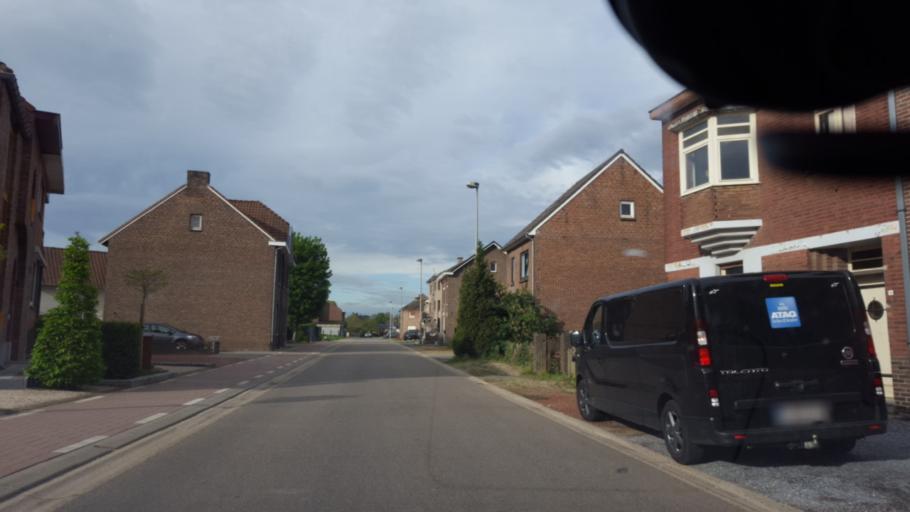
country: BE
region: Flanders
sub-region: Provincie Limburg
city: Maasmechelen
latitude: 50.9217
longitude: 5.6946
